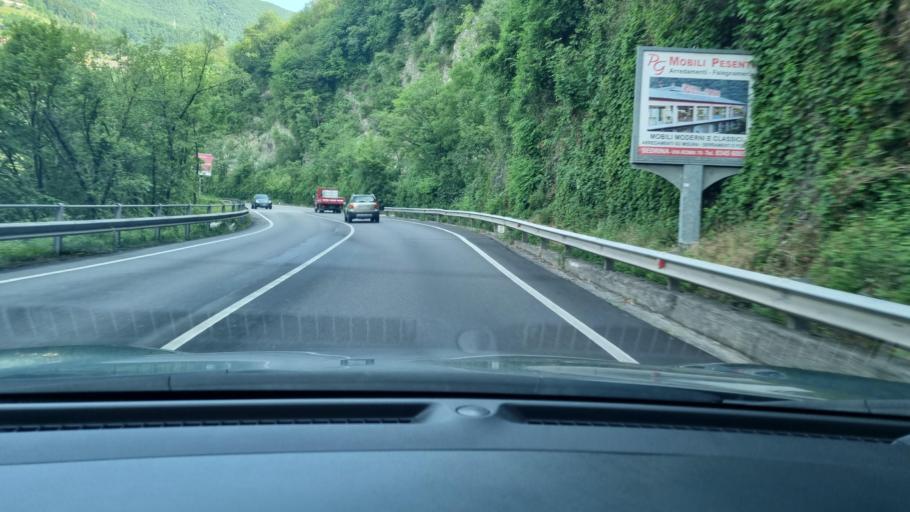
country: IT
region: Lombardy
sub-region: Provincia di Bergamo
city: Ubiale
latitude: 45.7739
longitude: 9.6150
